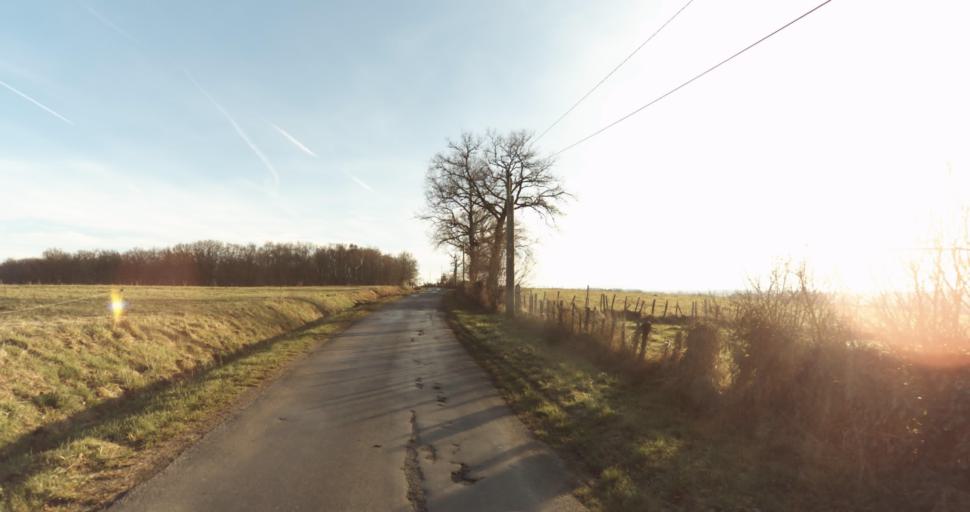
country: FR
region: Limousin
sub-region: Departement de la Haute-Vienne
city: Aixe-sur-Vienne
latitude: 45.7773
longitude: 1.1416
